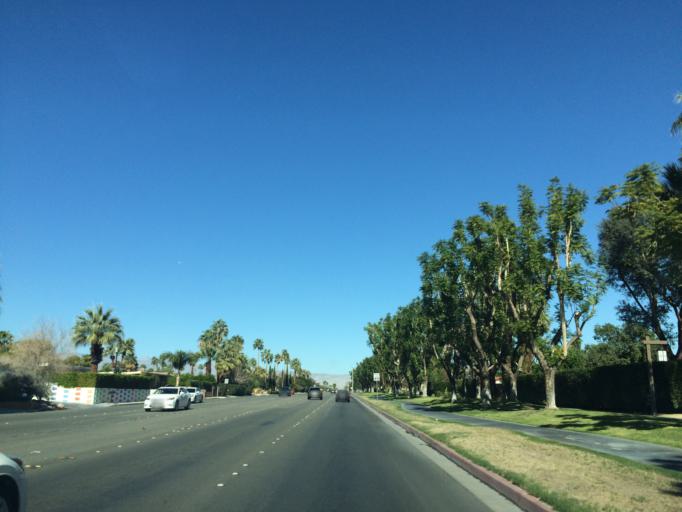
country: US
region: California
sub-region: Riverside County
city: Palm Springs
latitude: 33.8378
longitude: -116.5281
